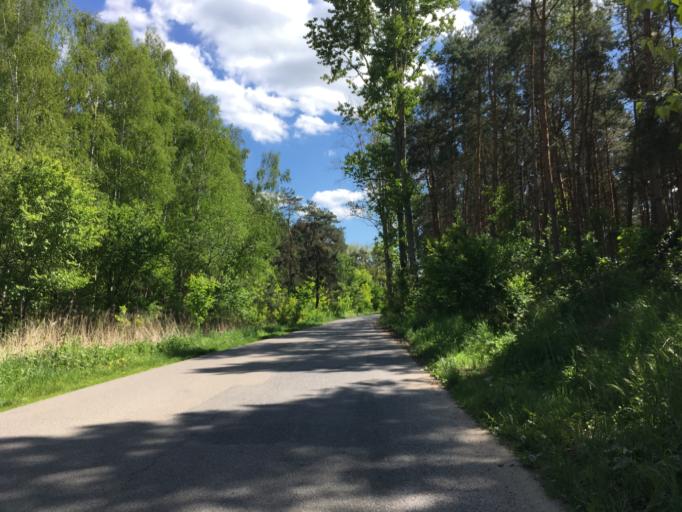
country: DE
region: Brandenburg
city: Rudnitz
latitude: 52.6977
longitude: 13.6675
